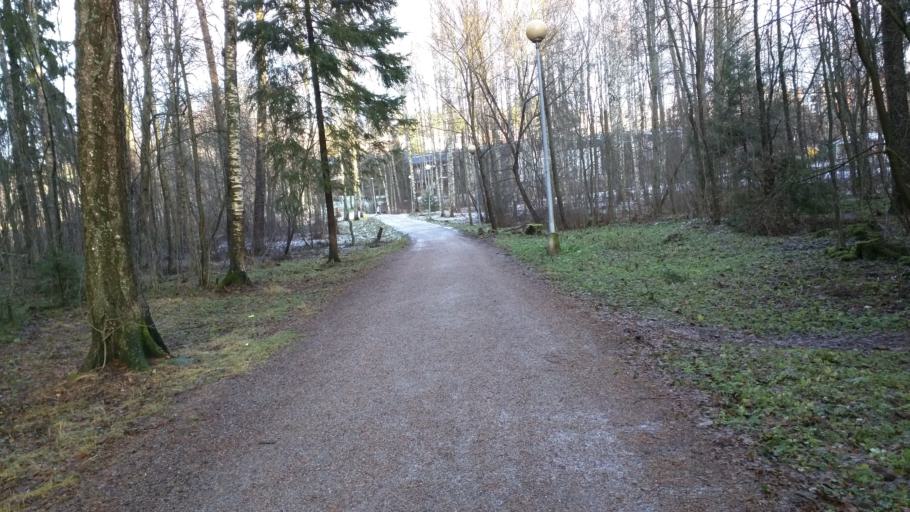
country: FI
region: Uusimaa
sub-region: Helsinki
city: Kilo
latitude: 60.2582
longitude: 24.8014
